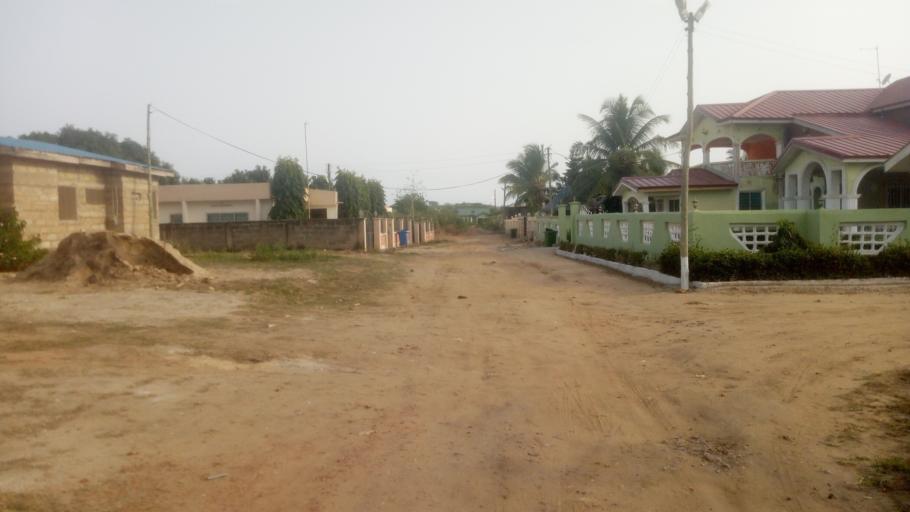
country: GH
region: Central
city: Winneba
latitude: 5.3767
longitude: -0.6294
